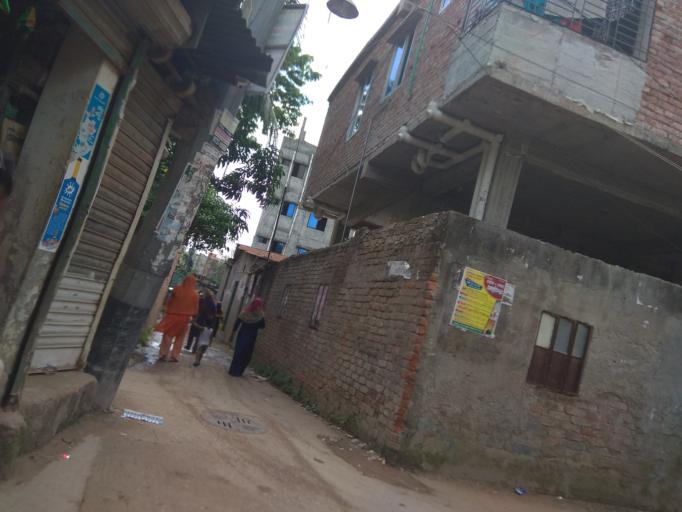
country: BD
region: Dhaka
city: Tungi
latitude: 23.8148
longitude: 90.3895
